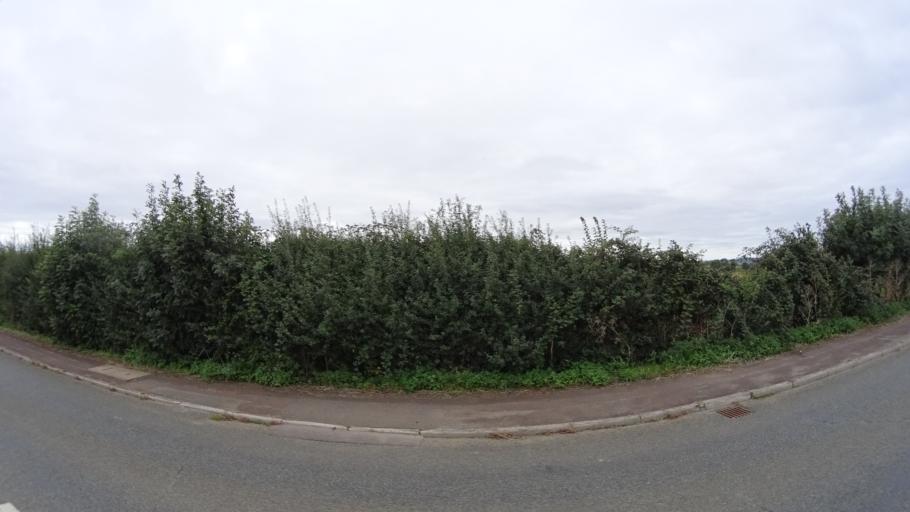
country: GB
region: England
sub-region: Somerset
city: Ilchester
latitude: 51.0109
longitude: -2.6640
